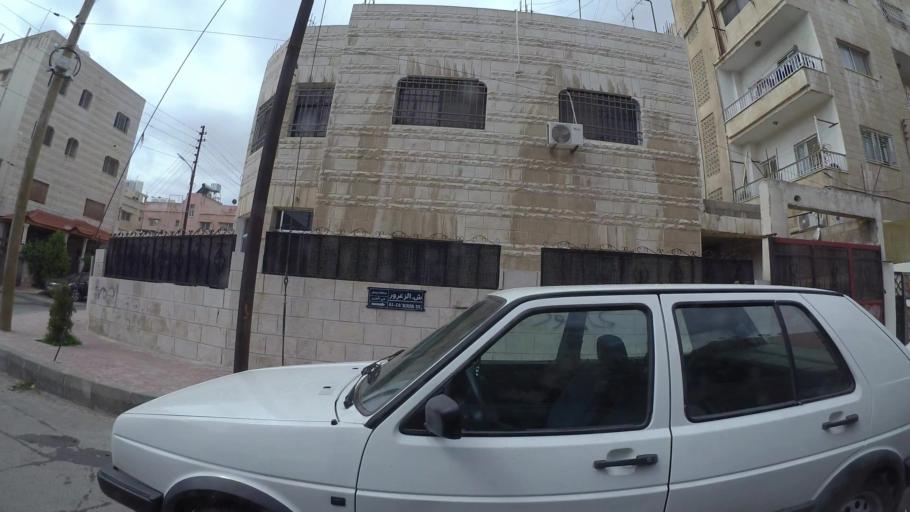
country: JO
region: Amman
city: Amman
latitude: 31.9826
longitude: 35.9218
